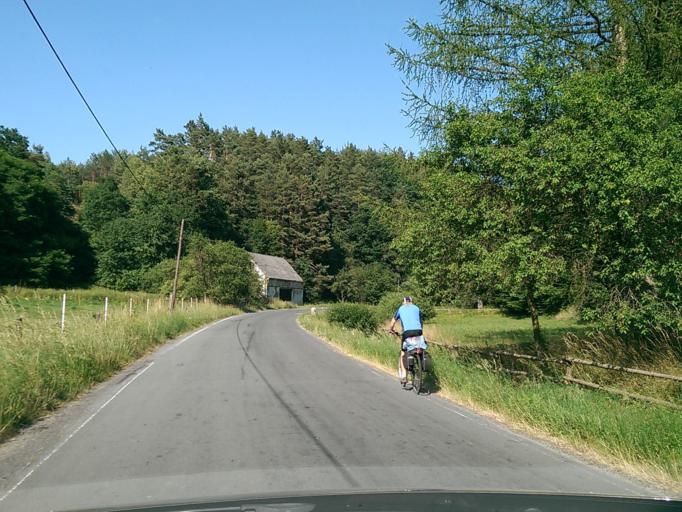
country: CZ
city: Duba
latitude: 50.5468
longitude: 14.4947
